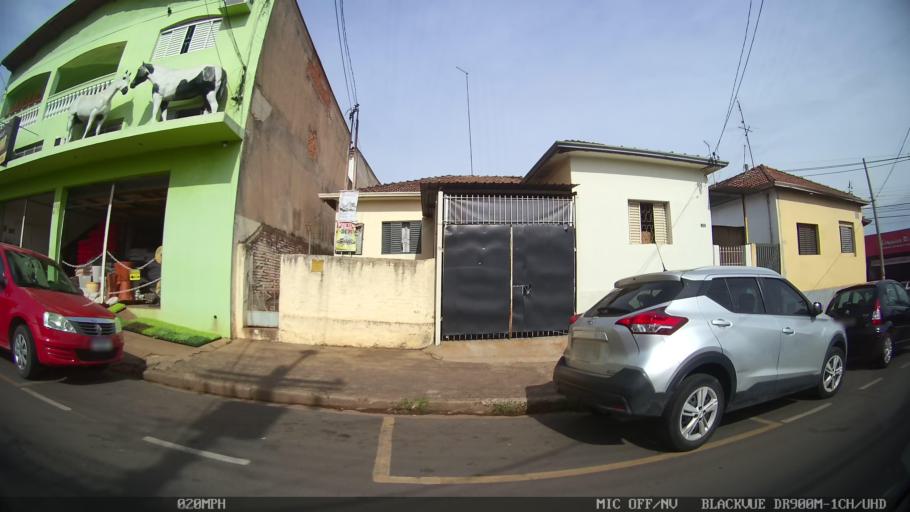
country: BR
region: Sao Paulo
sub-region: Piracicaba
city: Piracicaba
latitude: -22.7389
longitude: -47.6619
